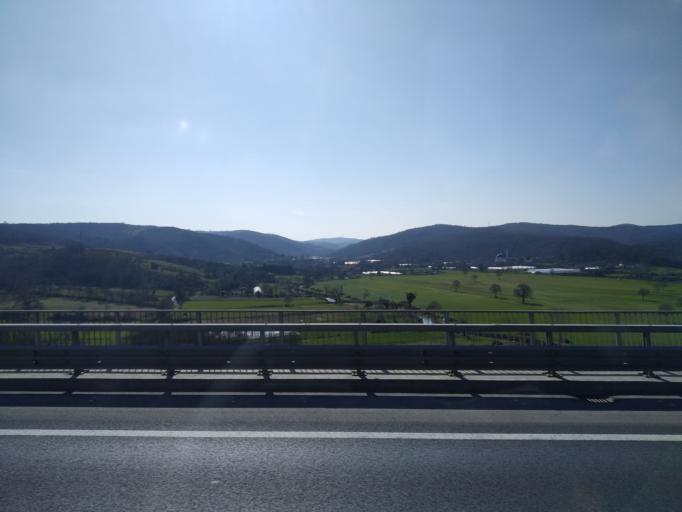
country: TR
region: Istanbul
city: Mahmut Sevket Pasa
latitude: 41.1875
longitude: 29.2132
